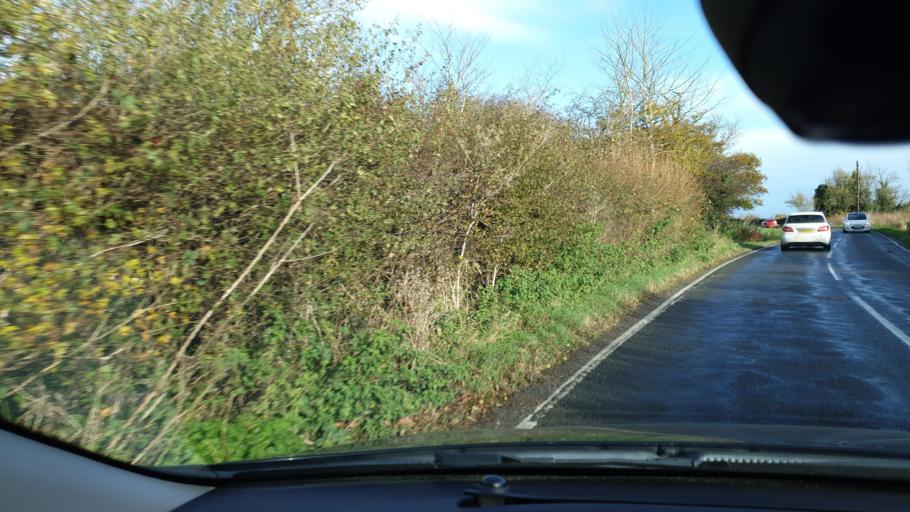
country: GB
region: England
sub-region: Essex
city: Dovercourt
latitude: 51.9100
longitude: 1.2165
